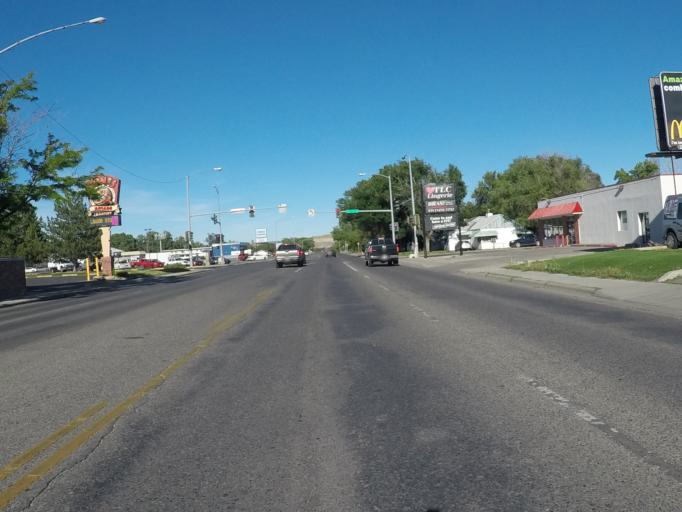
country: US
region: Montana
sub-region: Yellowstone County
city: Billings
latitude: 45.7770
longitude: -108.5522
